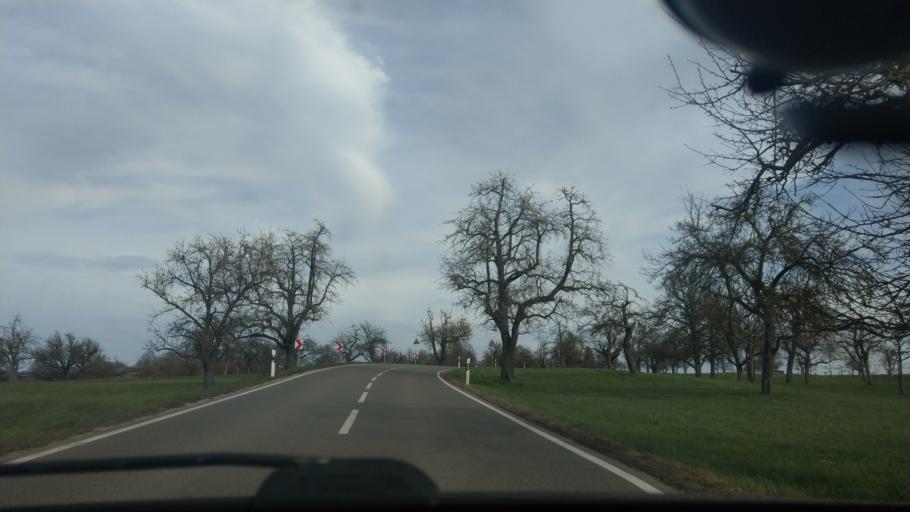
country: DE
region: Baden-Wuerttemberg
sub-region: Regierungsbezirk Stuttgart
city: Wolfschlugen
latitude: 48.6658
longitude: 9.2544
